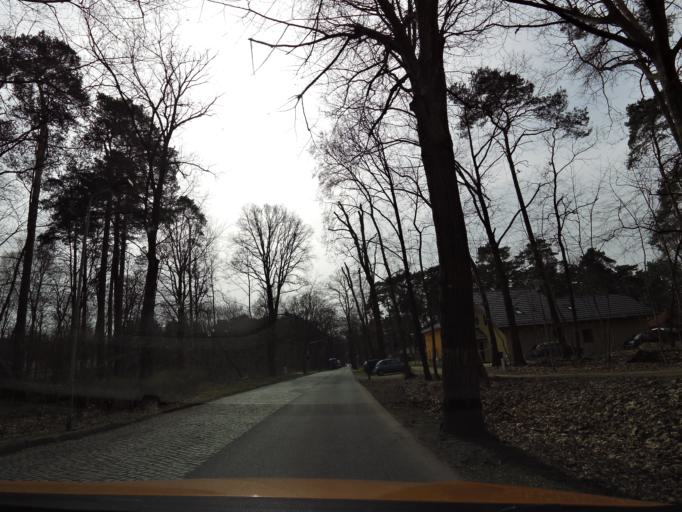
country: DE
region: Brandenburg
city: Rangsdorf
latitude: 52.3261
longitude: 13.3916
